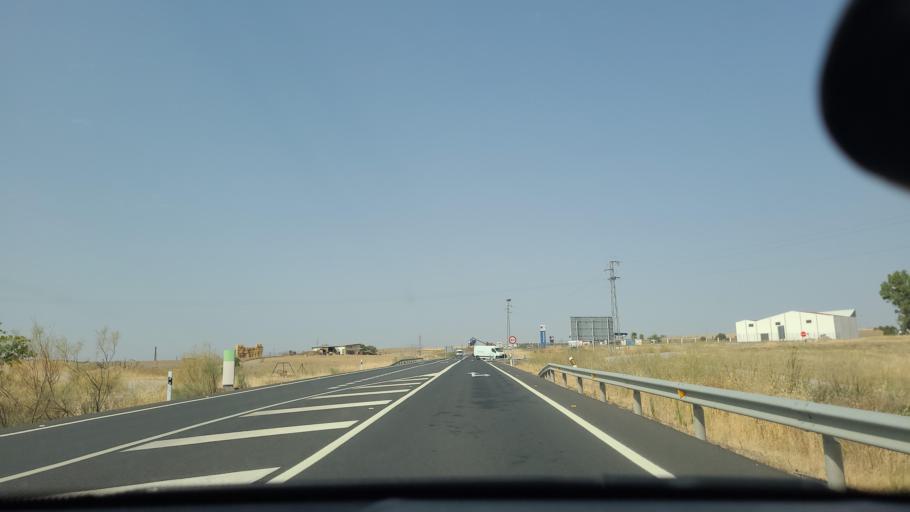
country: ES
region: Extremadura
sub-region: Provincia de Badajoz
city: Berlanga
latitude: 38.2753
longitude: -5.8271
